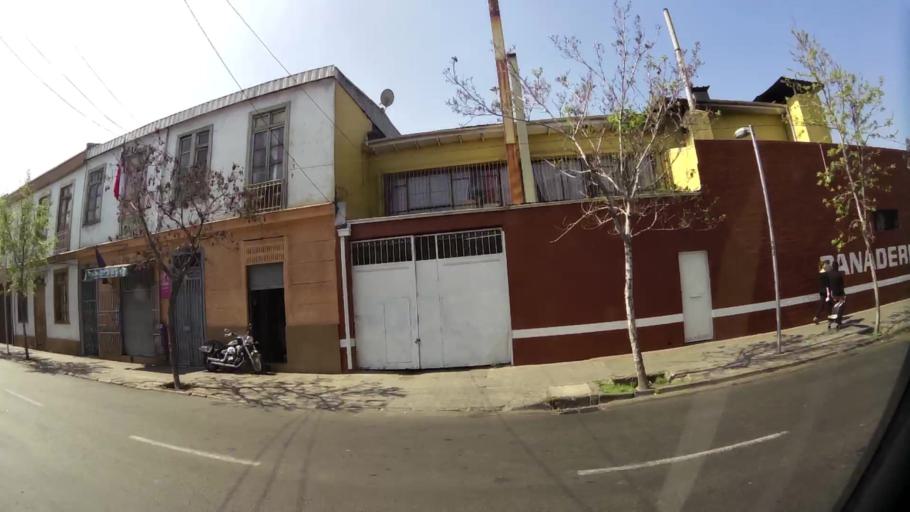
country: CL
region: Santiago Metropolitan
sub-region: Provincia de Santiago
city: Santiago
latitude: -33.4661
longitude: -70.6730
